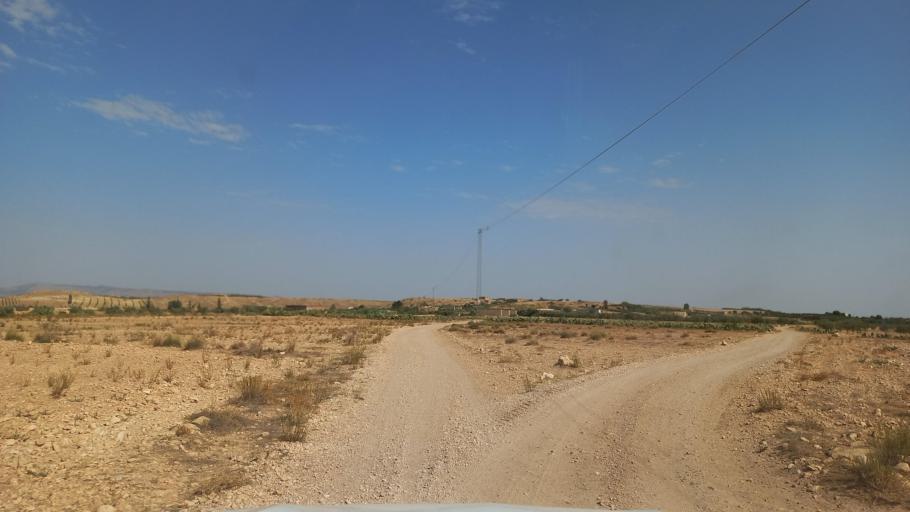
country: TN
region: Al Qasrayn
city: Kasserine
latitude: 35.2791
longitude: 8.9635
